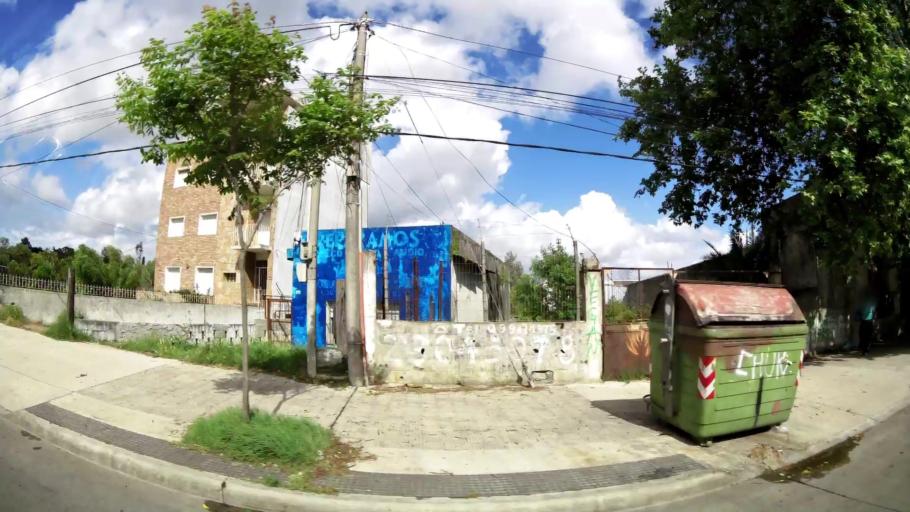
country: UY
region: Montevideo
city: Montevideo
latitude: -34.8469
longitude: -56.2227
